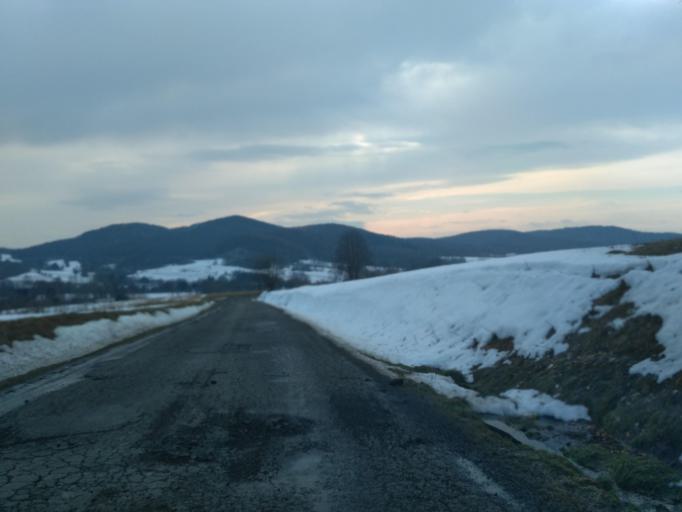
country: PL
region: Subcarpathian Voivodeship
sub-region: Powiat brzozowski
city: Dydnia
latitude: 49.6399
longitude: 22.1634
